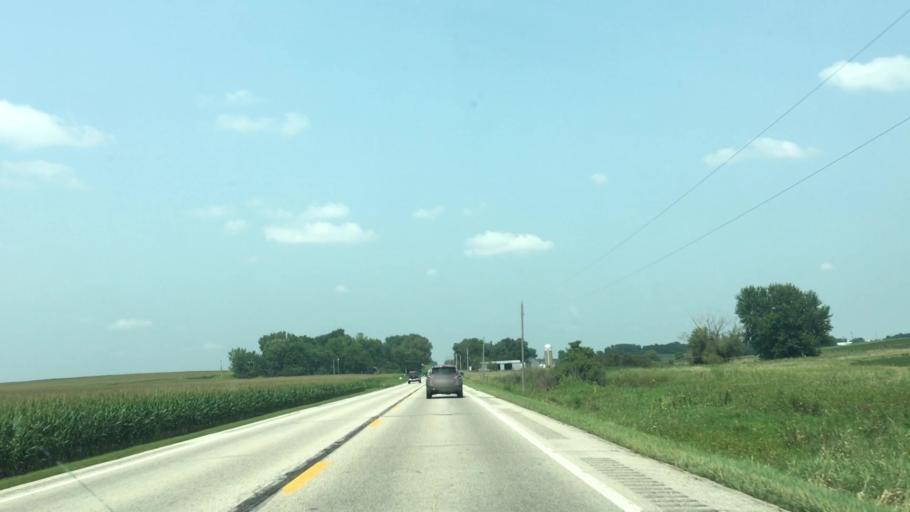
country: US
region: Iowa
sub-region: Buchanan County
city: Independence
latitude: 42.5252
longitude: -91.8899
